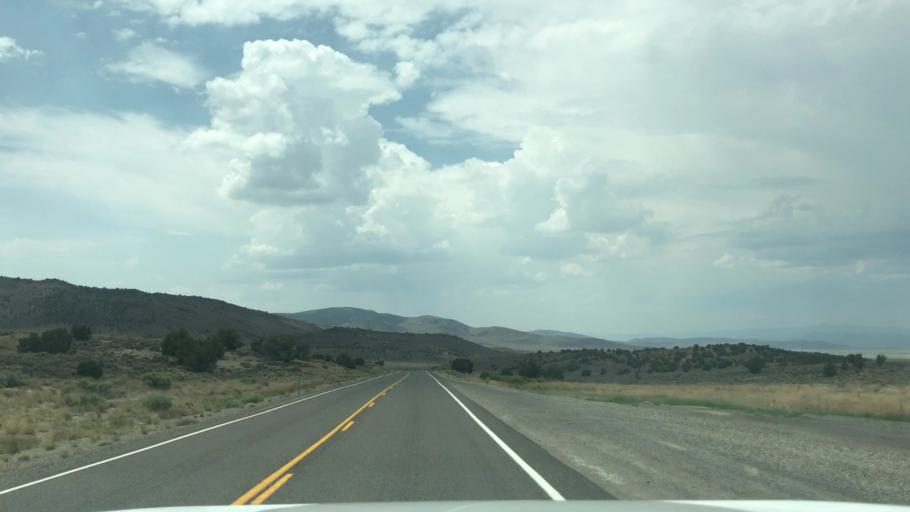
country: US
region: Nevada
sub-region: Eureka County
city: Eureka
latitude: 39.4067
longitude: -115.6992
